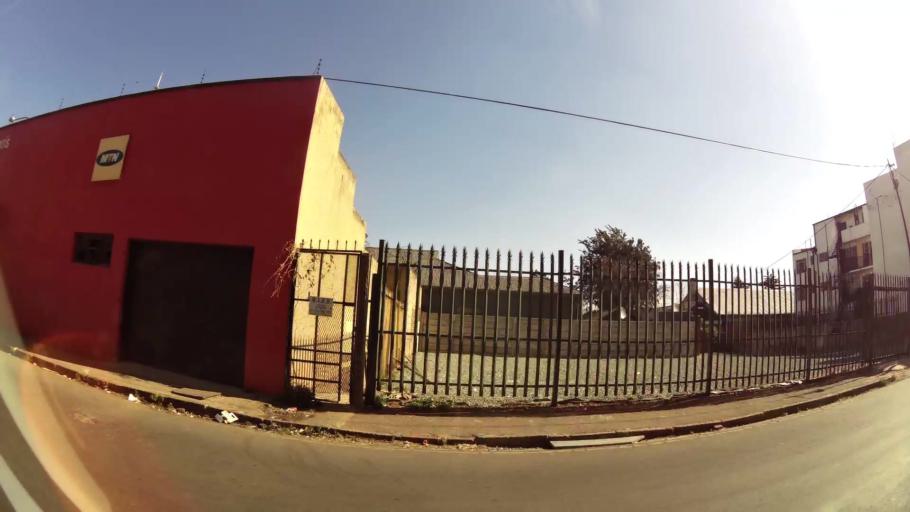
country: ZA
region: Gauteng
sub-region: City of Johannesburg Metropolitan Municipality
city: Johannesburg
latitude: -26.2020
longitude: 28.0709
